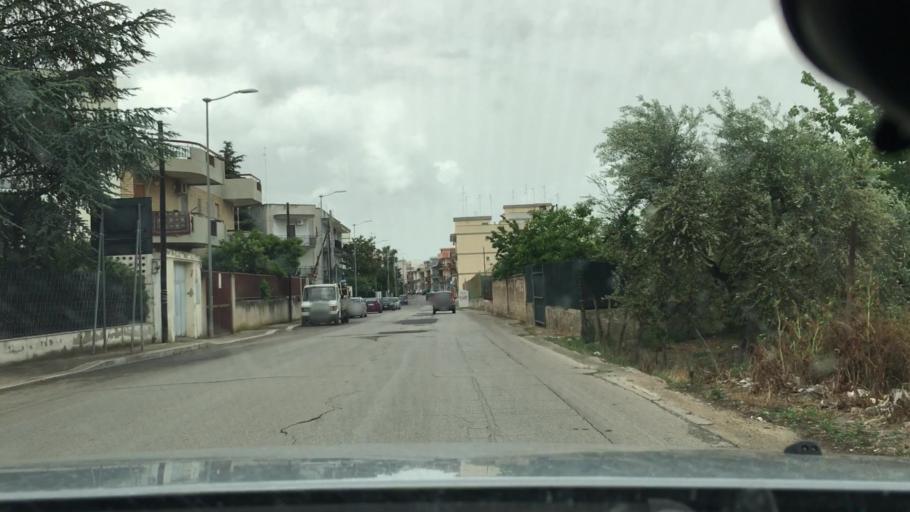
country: IT
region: Apulia
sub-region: Provincia di Bari
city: Capurso
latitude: 41.0455
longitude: 16.9292
